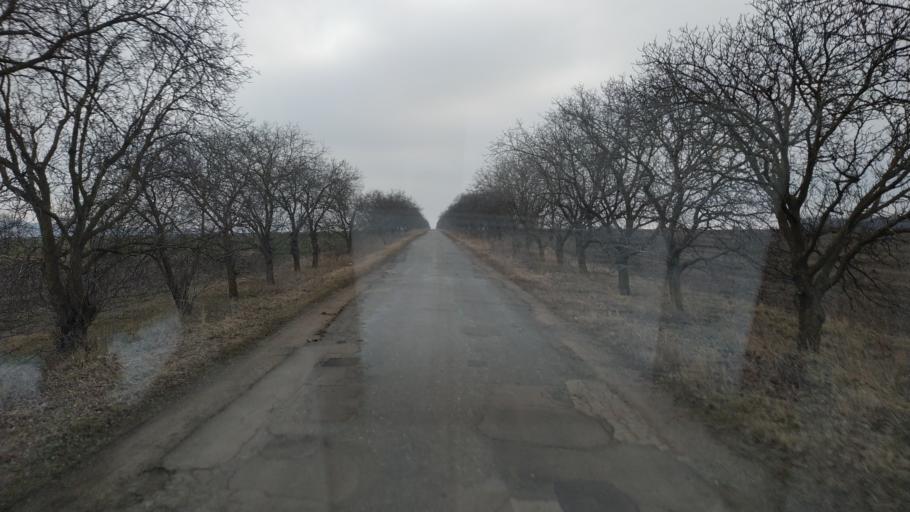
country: MD
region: Hincesti
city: Dancu
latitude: 46.8987
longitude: 28.3045
